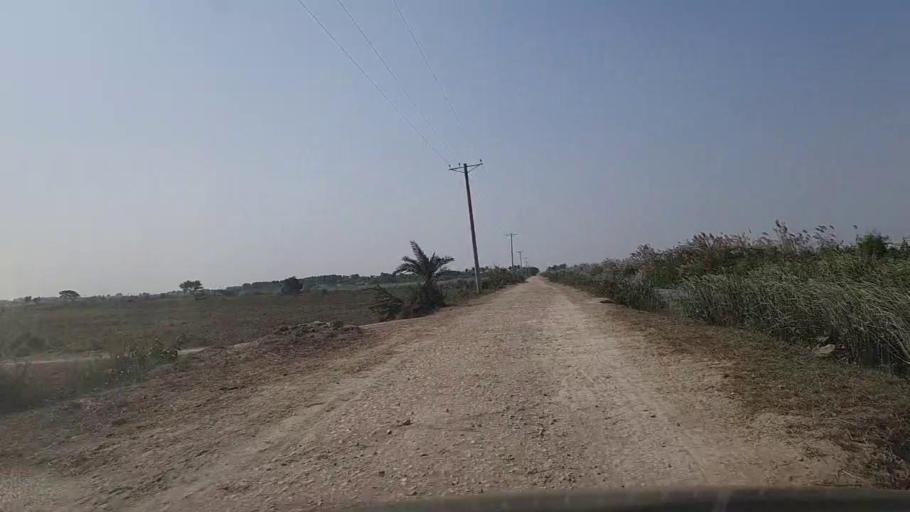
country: PK
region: Sindh
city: Gharo
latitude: 24.6823
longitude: 67.5987
